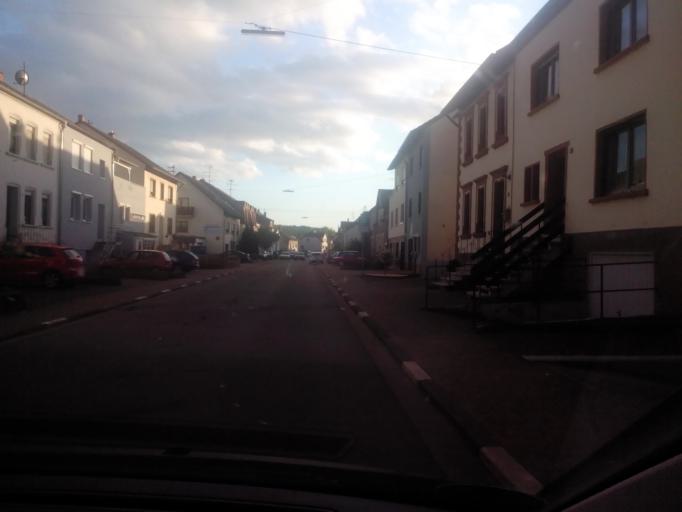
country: DE
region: Saarland
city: Saarwellingen
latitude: 49.3899
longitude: 6.8340
